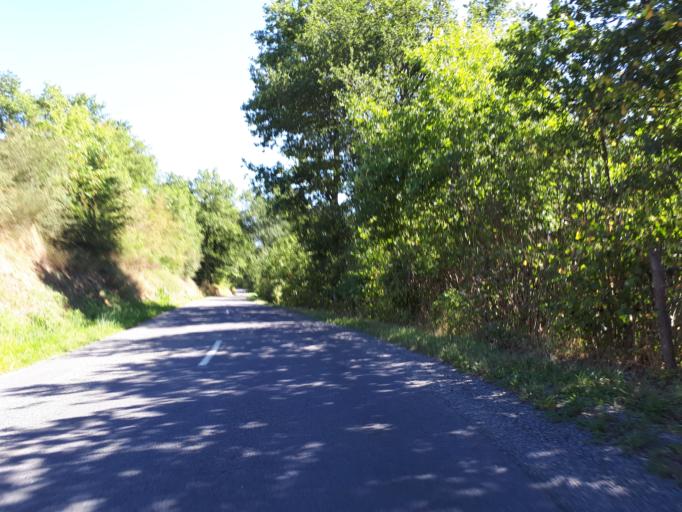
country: FR
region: Rhone-Alpes
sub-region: Departement de la Loire
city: Pouilly-les-Feurs
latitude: 45.8182
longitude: 4.2497
